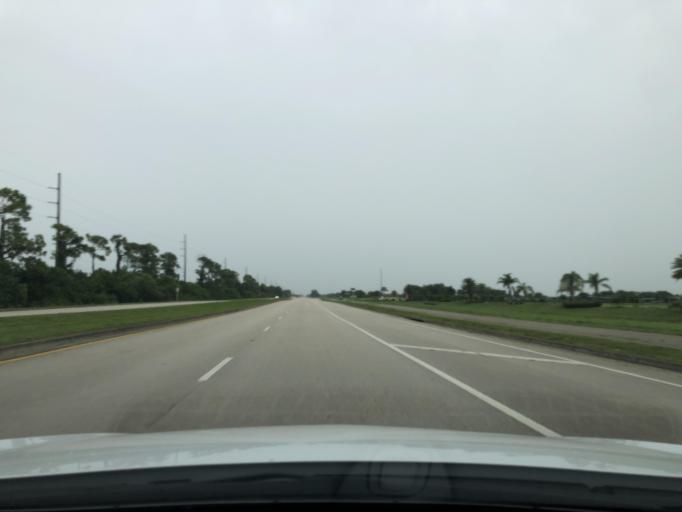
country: US
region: Florida
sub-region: Collier County
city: Immokalee
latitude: 26.2949
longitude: -81.4273
